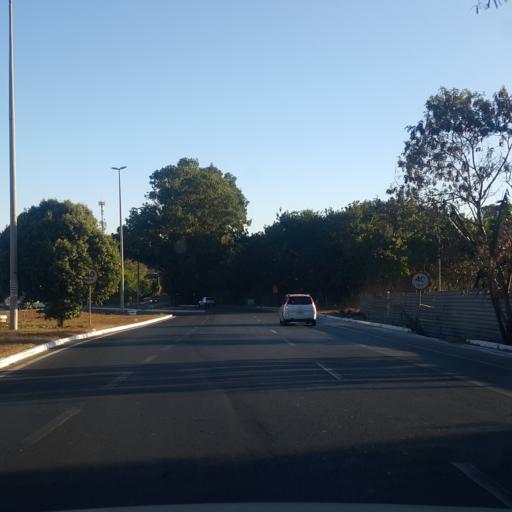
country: BR
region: Federal District
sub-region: Brasilia
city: Brasilia
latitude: -15.8563
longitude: -47.9762
